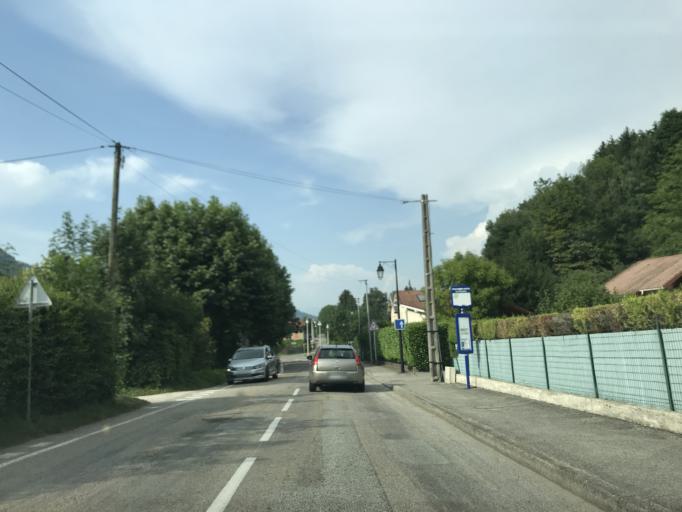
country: FR
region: Rhone-Alpes
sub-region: Departement de l'Isere
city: Allevard
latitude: 45.4006
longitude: 6.0809
